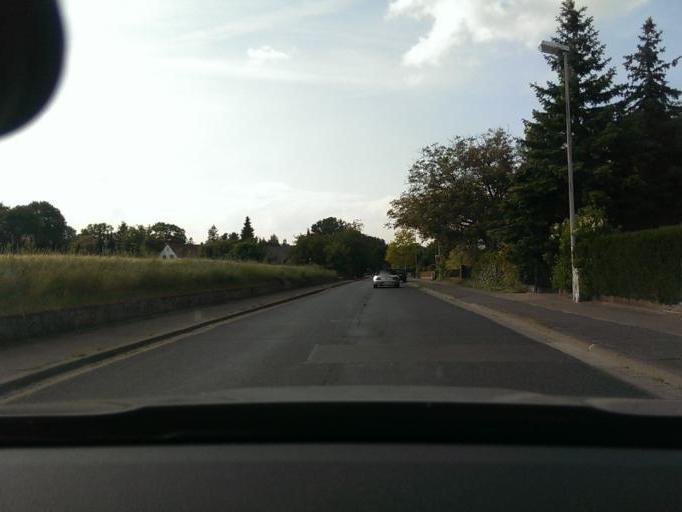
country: DE
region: Lower Saxony
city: Elze
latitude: 52.5607
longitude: 9.7270
